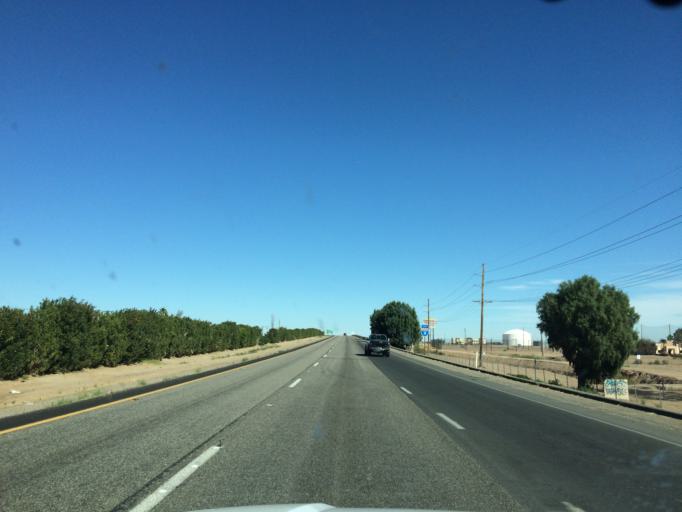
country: US
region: California
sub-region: Imperial County
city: El Centro
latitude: 32.7736
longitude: -115.5485
